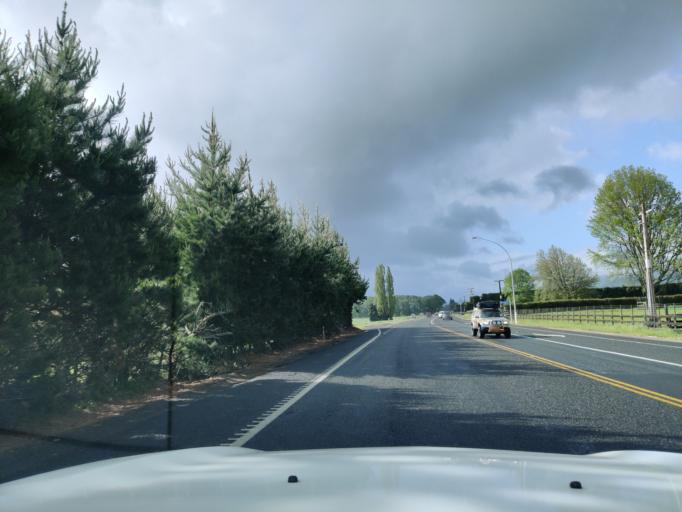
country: NZ
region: Waikato
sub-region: Waipa District
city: Cambridge
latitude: -37.9288
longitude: 175.5706
